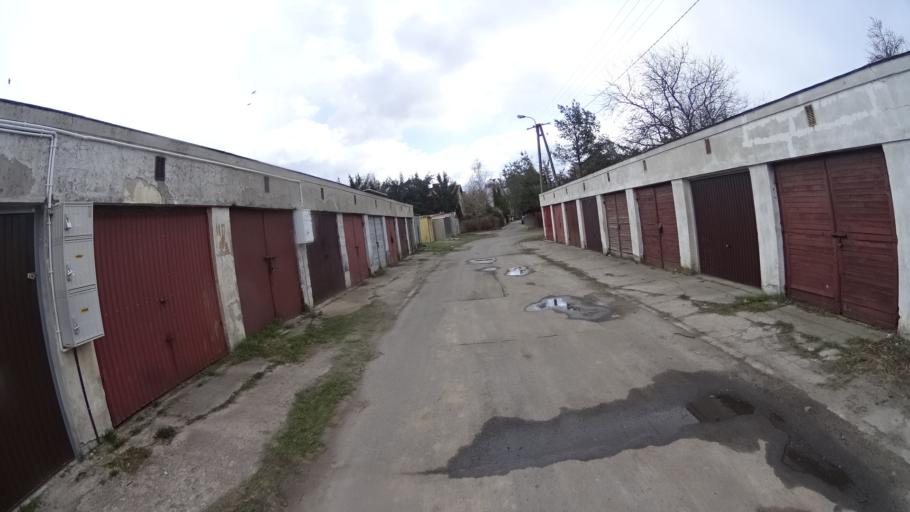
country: PL
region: Masovian Voivodeship
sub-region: Powiat warszawski zachodni
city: Blonie
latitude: 52.2185
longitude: 20.6478
